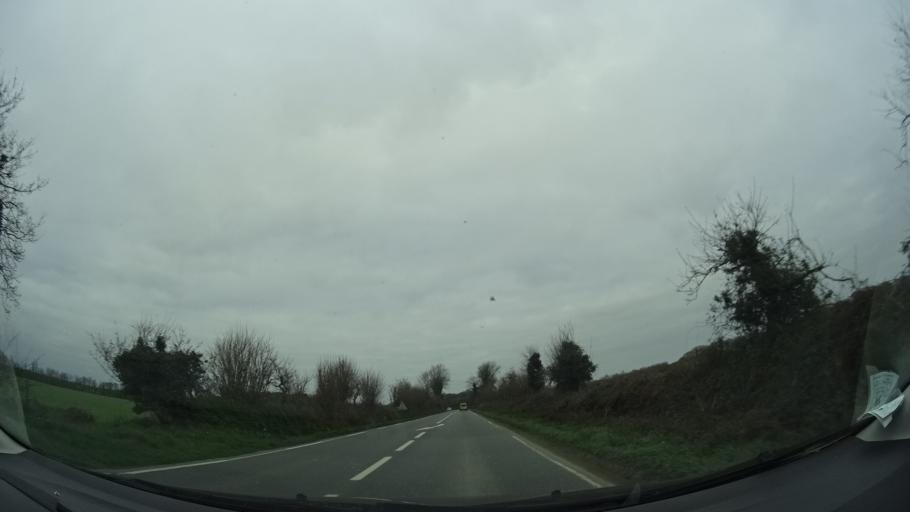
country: FR
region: Brittany
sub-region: Departement du Finistere
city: Guilers
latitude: 48.4387
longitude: -4.5650
